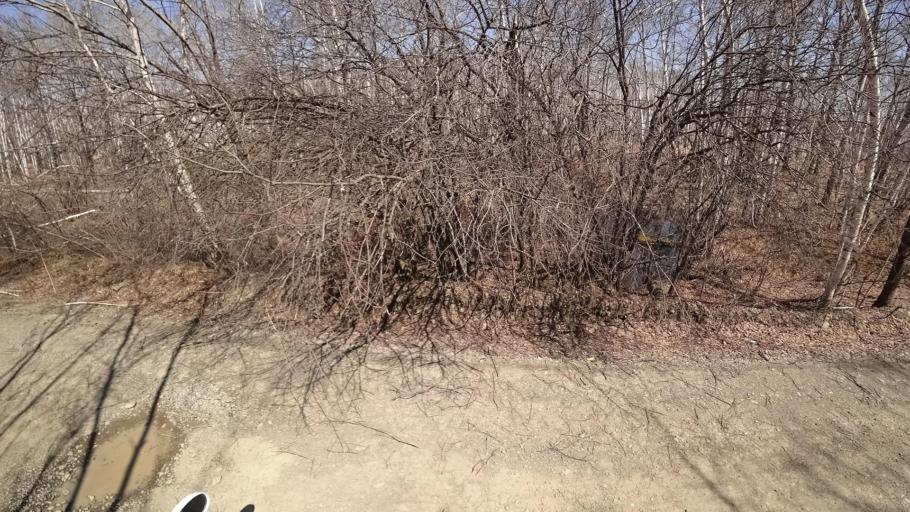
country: RU
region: Khabarovsk Krai
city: Khurba
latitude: 50.4180
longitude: 136.8355
